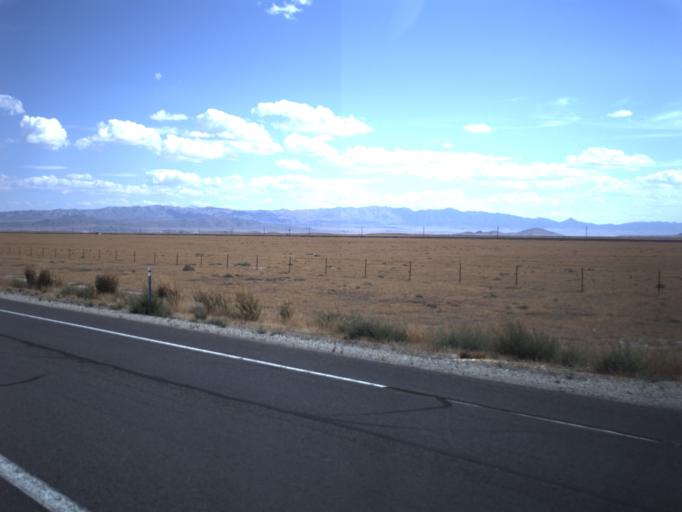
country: US
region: Utah
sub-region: Tooele County
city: Wendover
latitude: 40.7264
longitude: -113.2514
